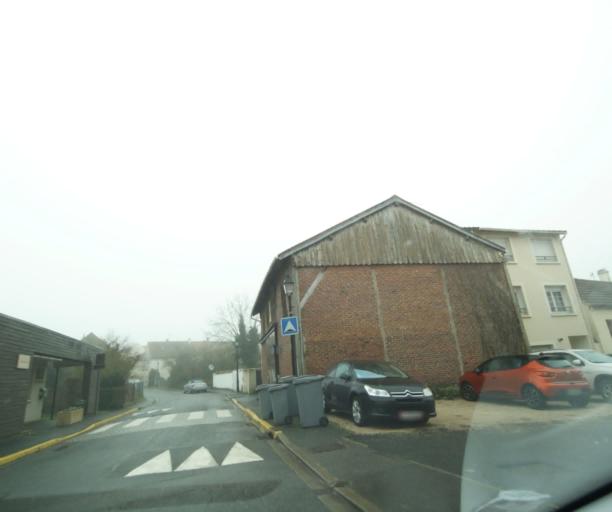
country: FR
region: Ile-de-France
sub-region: Departement de Seine-et-Marne
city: Longperrier
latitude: 49.0501
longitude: 2.6647
